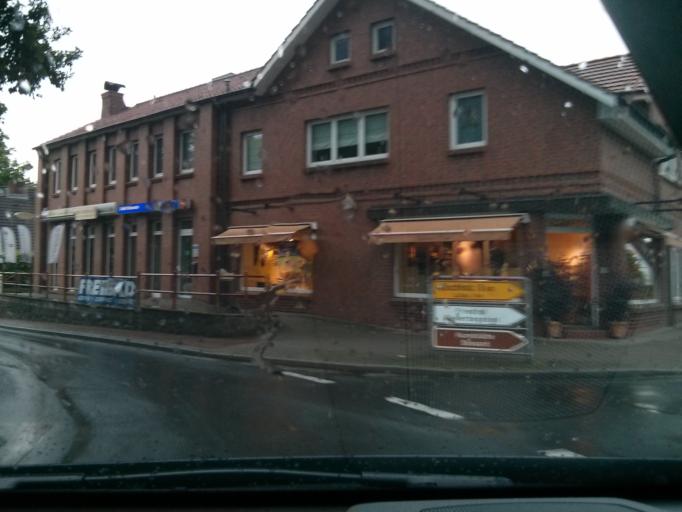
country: DE
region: Lower Saxony
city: Jesteburg
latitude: 53.3065
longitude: 9.9529
